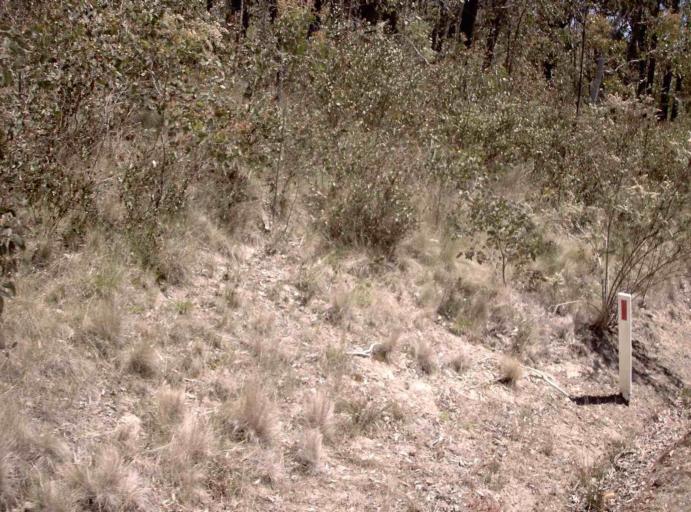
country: AU
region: New South Wales
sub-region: Snowy River
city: Jindabyne
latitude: -37.1102
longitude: 148.2515
